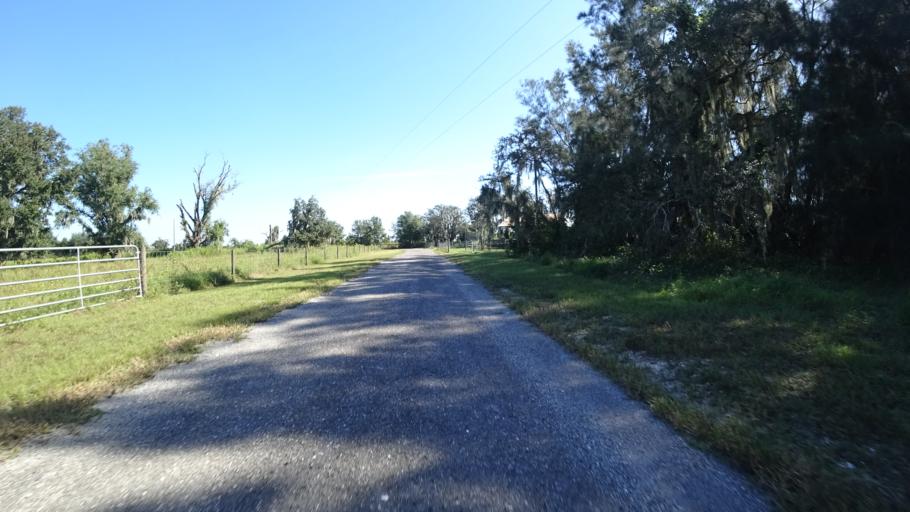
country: US
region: Florida
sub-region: Hillsborough County
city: Wimauma
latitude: 27.5983
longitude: -82.1870
